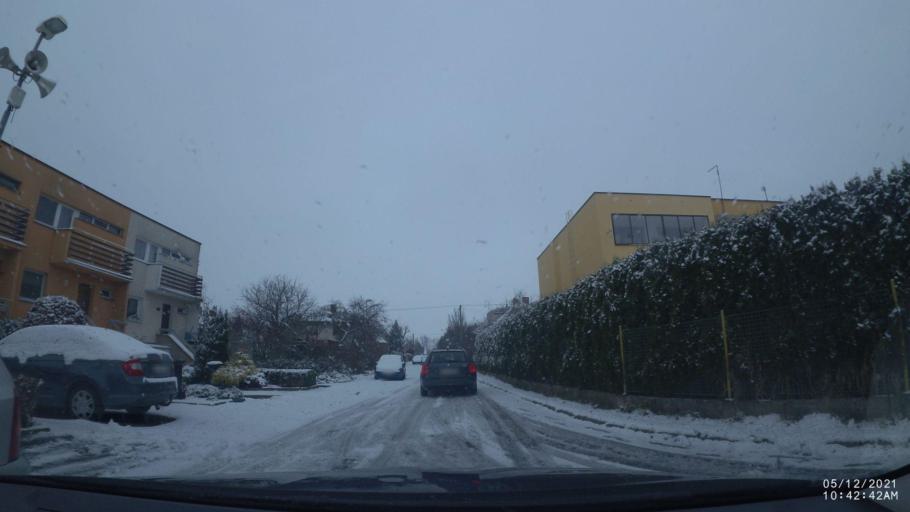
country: CZ
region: Kralovehradecky
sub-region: Okres Rychnov nad Kneznou
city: Rychnov nad Kneznou
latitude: 50.1669
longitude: 16.2848
